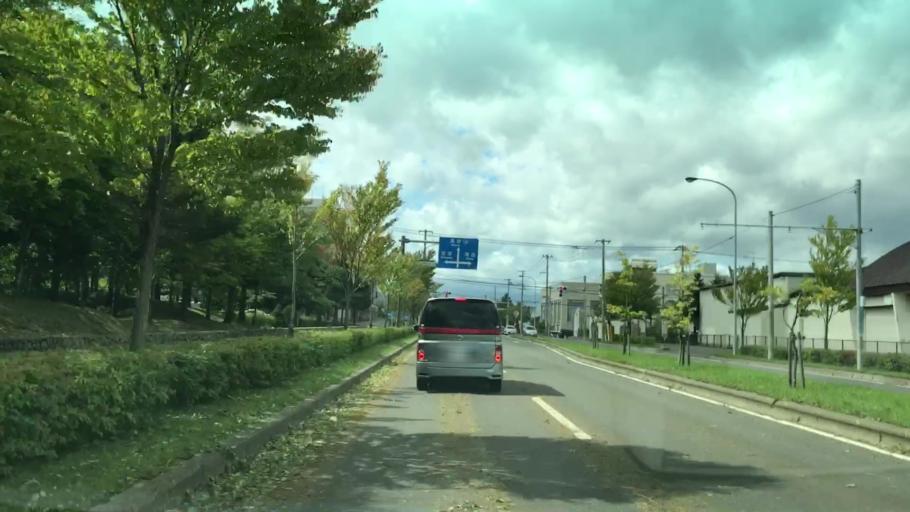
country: JP
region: Hokkaido
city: Kitahiroshima
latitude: 42.9922
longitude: 141.4547
